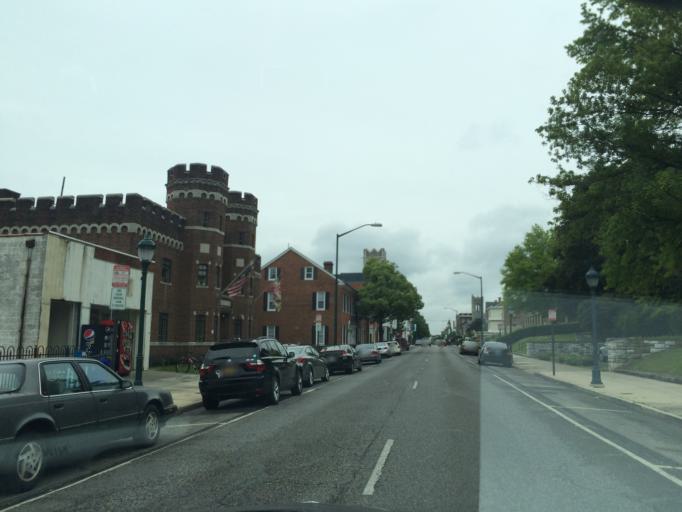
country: US
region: Maryland
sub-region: Washington County
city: Hagerstown
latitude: 39.6469
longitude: -77.7164
